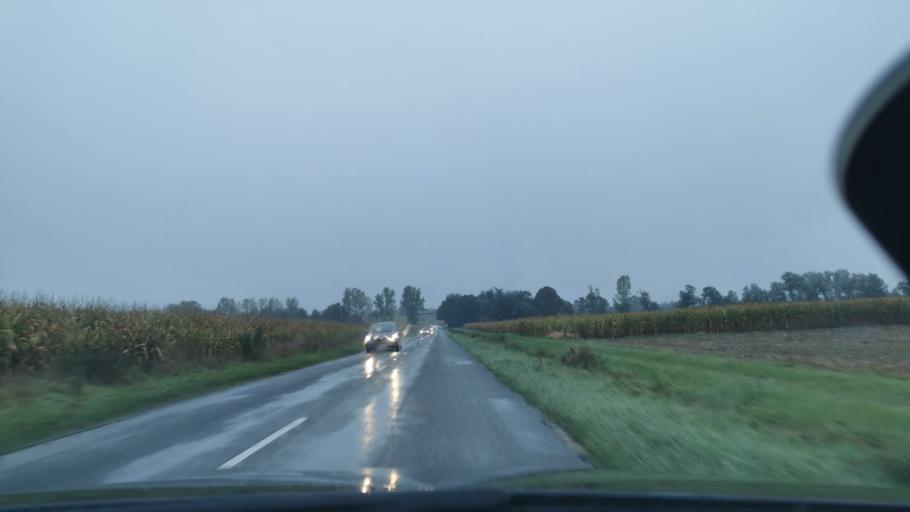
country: FR
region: Rhone-Alpes
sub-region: Departement de l'Ain
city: Civrieux
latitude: 45.9439
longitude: 4.8828
